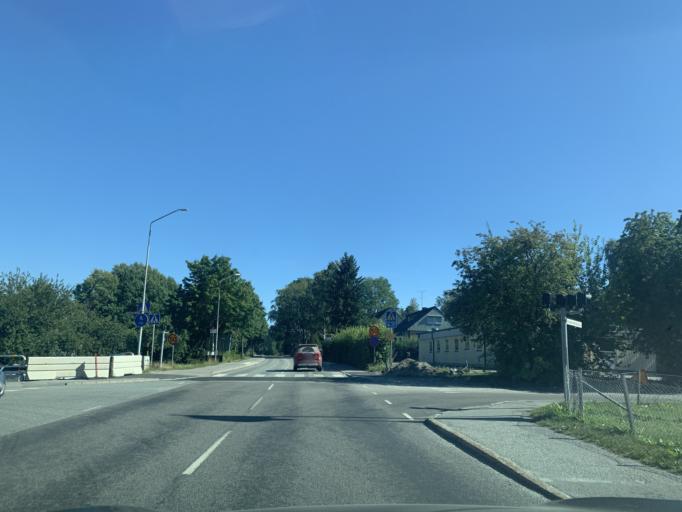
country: SE
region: Stockholm
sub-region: Ekero Kommun
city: Ekeroe
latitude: 59.2892
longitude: 17.8120
